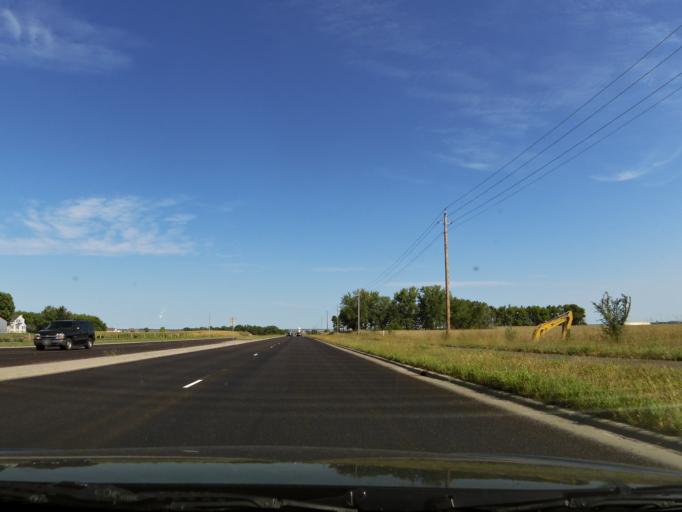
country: US
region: Minnesota
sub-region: Scott County
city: Prior Lake
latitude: 44.7562
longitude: -93.4695
